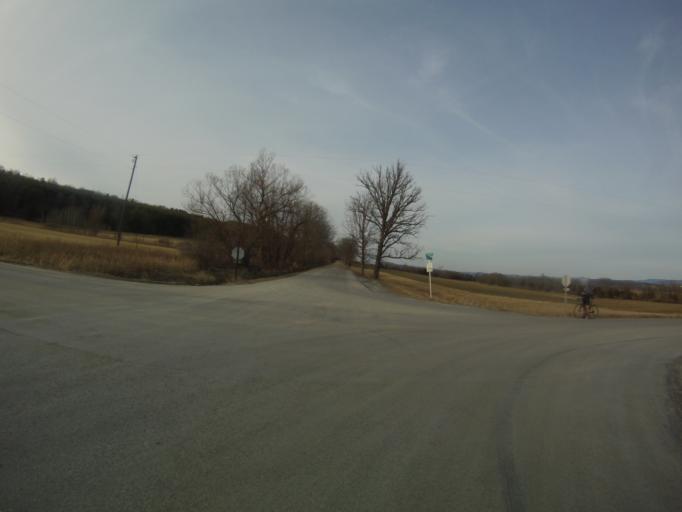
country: US
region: Vermont
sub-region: Addison County
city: Middlebury (village)
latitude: 44.0174
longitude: -73.2565
